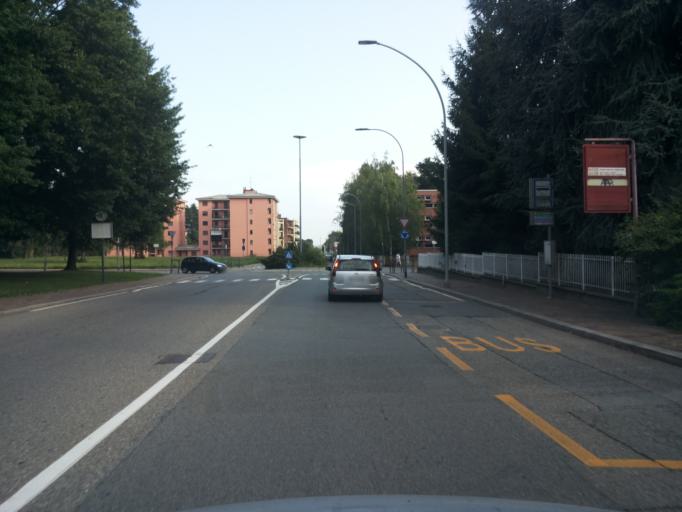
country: IT
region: Piedmont
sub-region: Provincia di Biella
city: Biella
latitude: 45.5562
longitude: 8.0545
